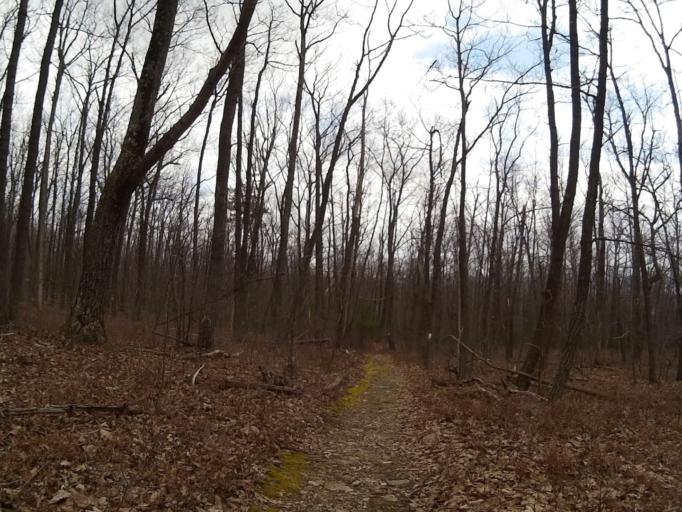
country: US
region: Pennsylvania
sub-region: Centre County
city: Lemont
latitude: 40.8104
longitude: -77.7952
